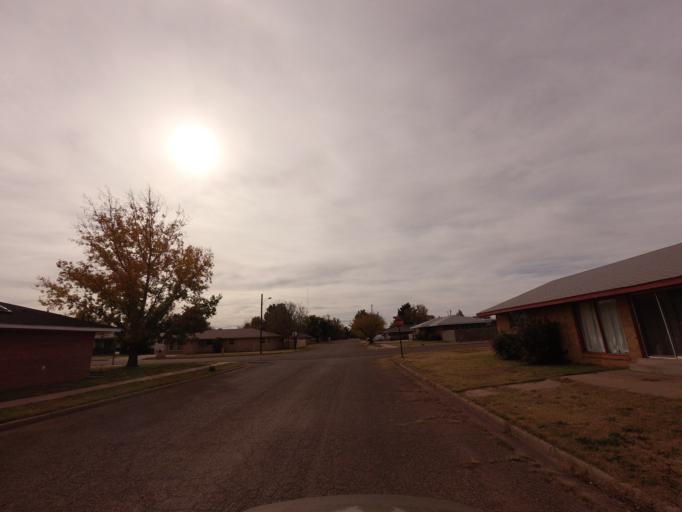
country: US
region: New Mexico
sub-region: Curry County
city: Clovis
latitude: 34.4249
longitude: -103.2096
